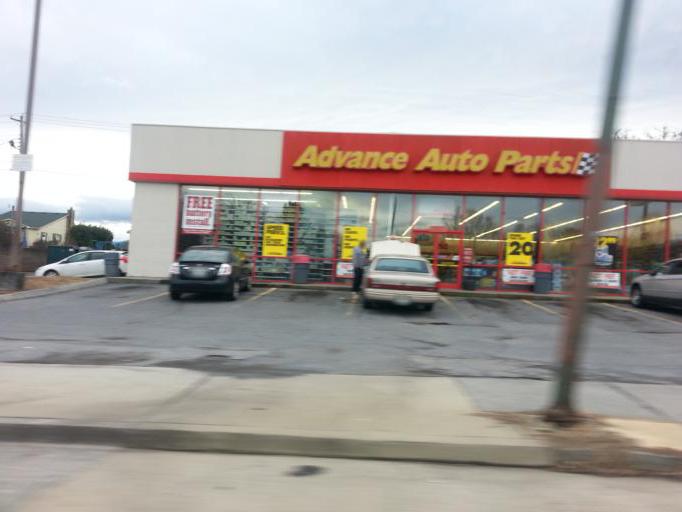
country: US
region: Tennessee
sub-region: Washington County
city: Johnson City
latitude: 36.3144
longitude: -82.3764
